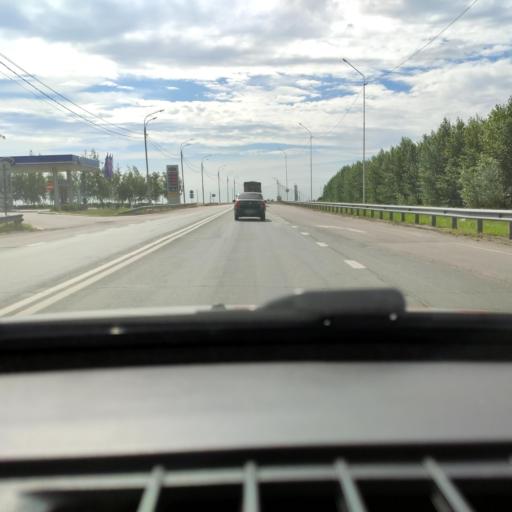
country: RU
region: Voronezj
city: Devitsa
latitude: 51.6320
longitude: 38.9869
